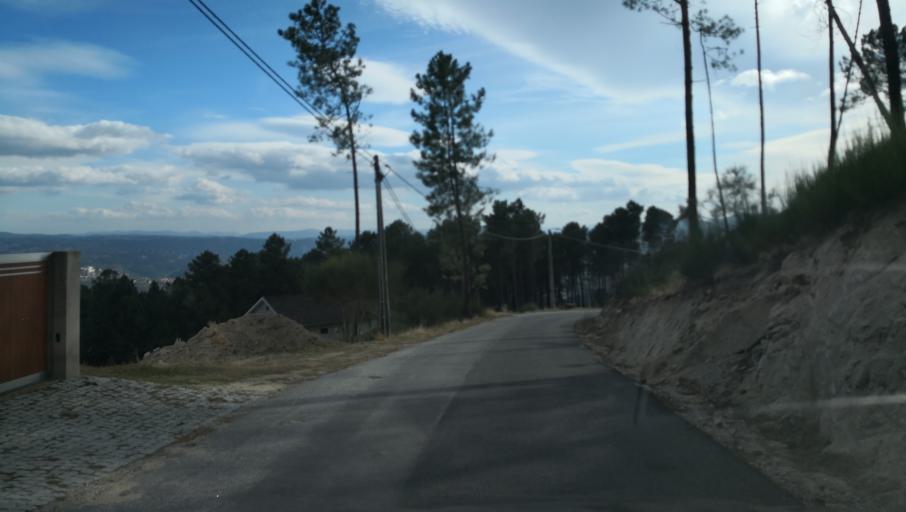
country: PT
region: Vila Real
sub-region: Vila Real
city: Vila Real
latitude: 41.3236
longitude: -7.7755
